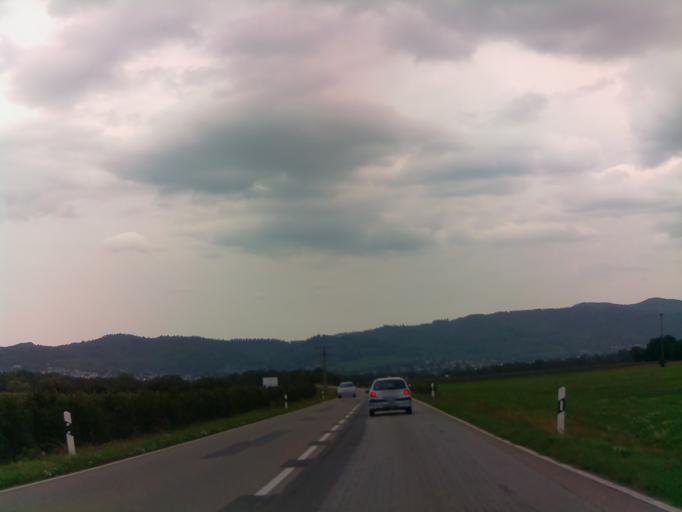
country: DE
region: Baden-Wuerttemberg
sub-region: Karlsruhe Region
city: Heddesheim
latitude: 49.5319
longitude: 8.6209
